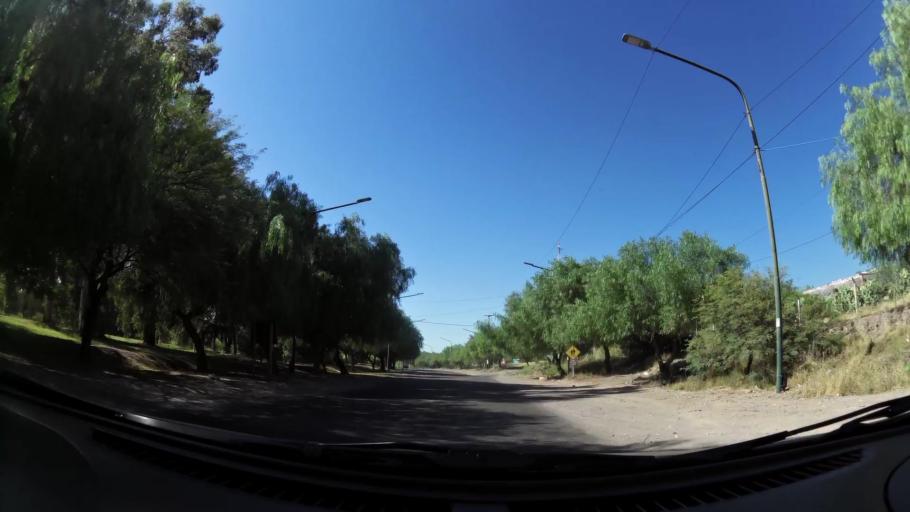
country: AR
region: Mendoza
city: Mendoza
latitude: -32.8927
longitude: -68.8845
